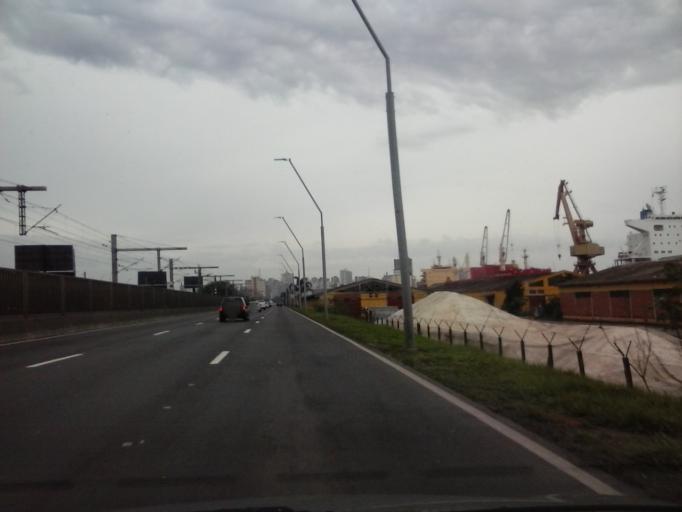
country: BR
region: Rio Grande do Sul
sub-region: Porto Alegre
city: Porto Alegre
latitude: -30.0123
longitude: -51.2126
